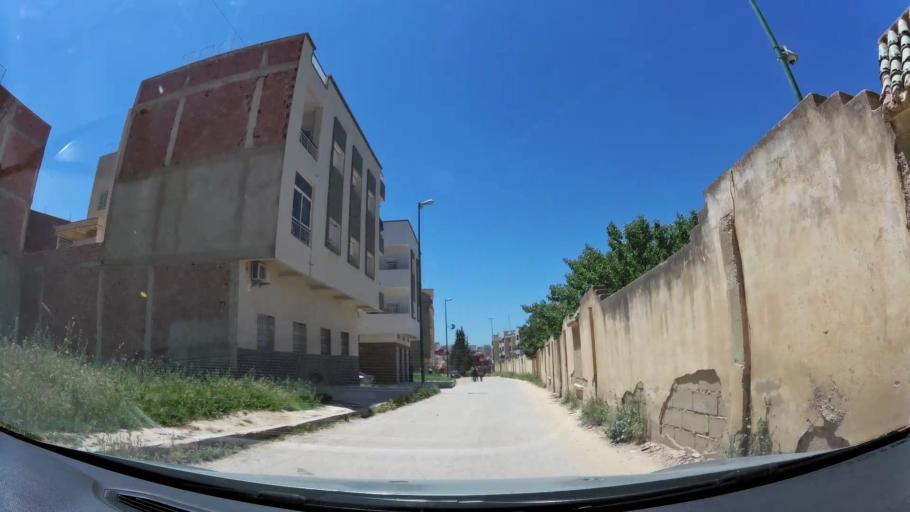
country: MA
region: Meknes-Tafilalet
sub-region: Meknes
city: Meknes
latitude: 33.8672
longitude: -5.5716
